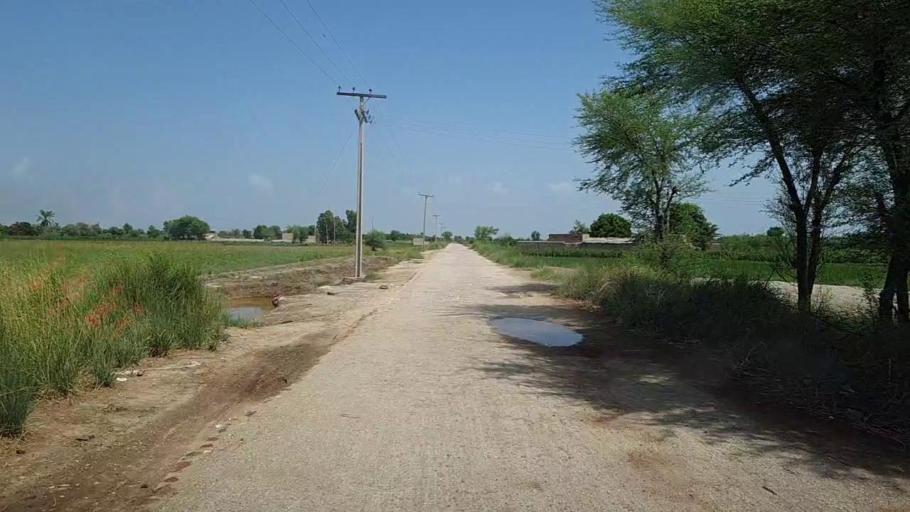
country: PK
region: Sindh
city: Bhiria
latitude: 26.8838
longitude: 68.2372
